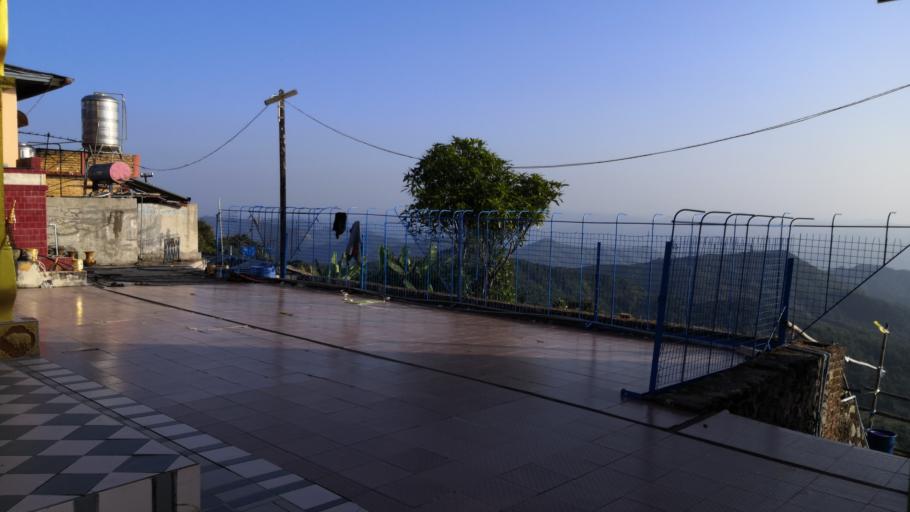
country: MM
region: Mandalay
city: Mogok
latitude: 22.8904
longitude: 96.4231
